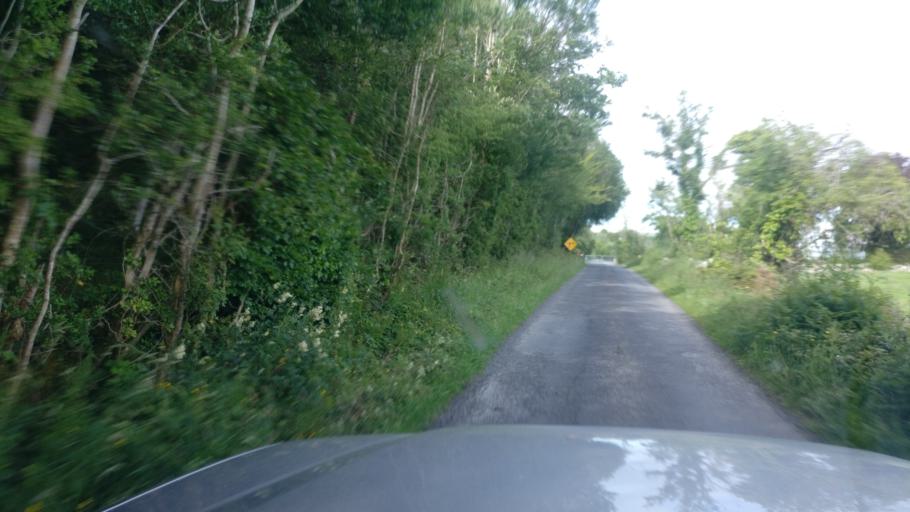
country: IE
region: Connaught
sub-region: County Galway
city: Gort
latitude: 53.1032
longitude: -8.7132
